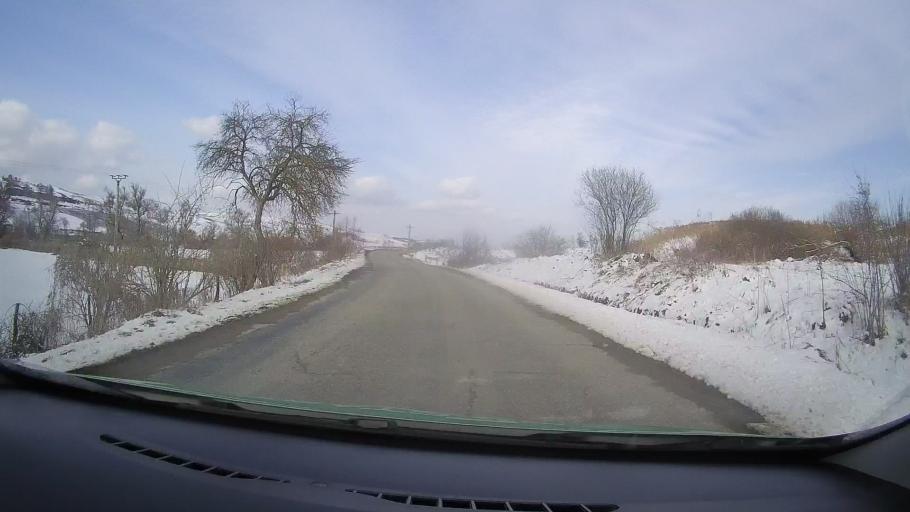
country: RO
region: Sibiu
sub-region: Oras Agnita
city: Ruja
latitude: 45.9851
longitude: 24.6580
